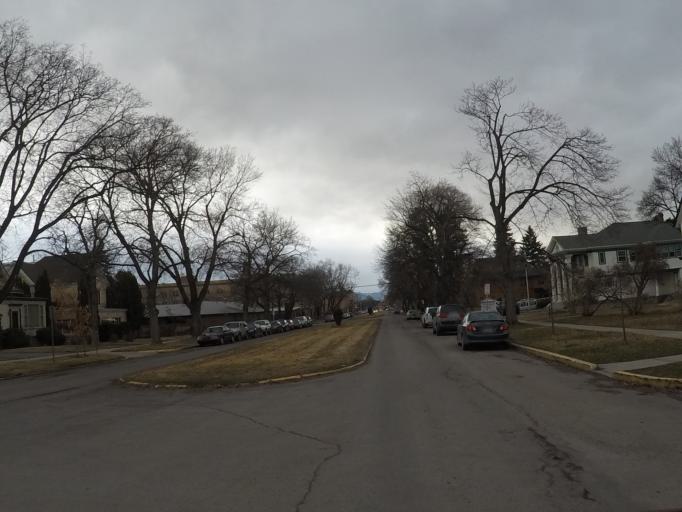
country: US
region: Montana
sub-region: Missoula County
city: Missoula
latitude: 46.8718
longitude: -113.9890
